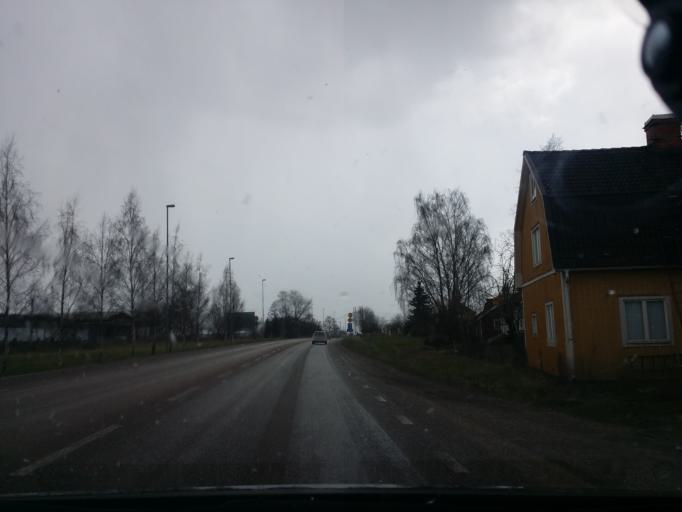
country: SE
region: Vaestmanland
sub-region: Sala Kommun
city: Sala
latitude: 59.9152
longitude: 16.6169
